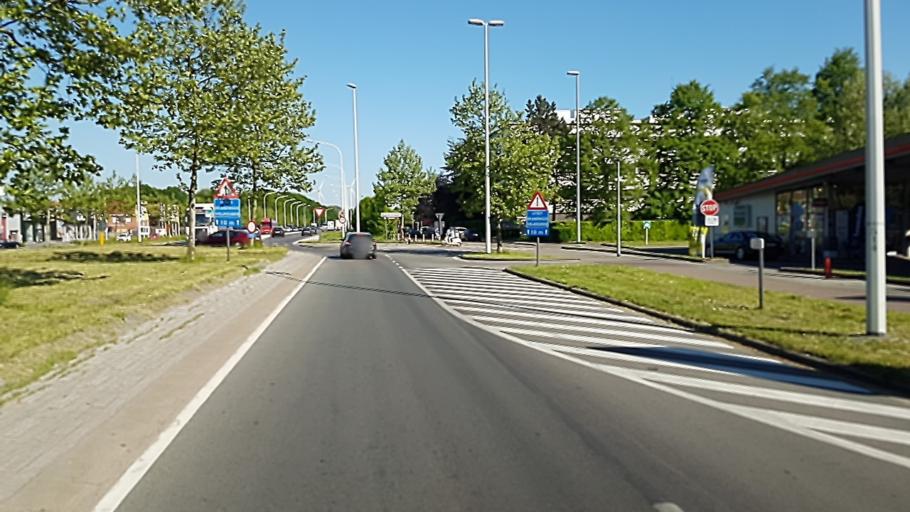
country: BE
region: Flanders
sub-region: Provincie Antwerpen
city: Herentals
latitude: 51.1870
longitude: 4.8392
